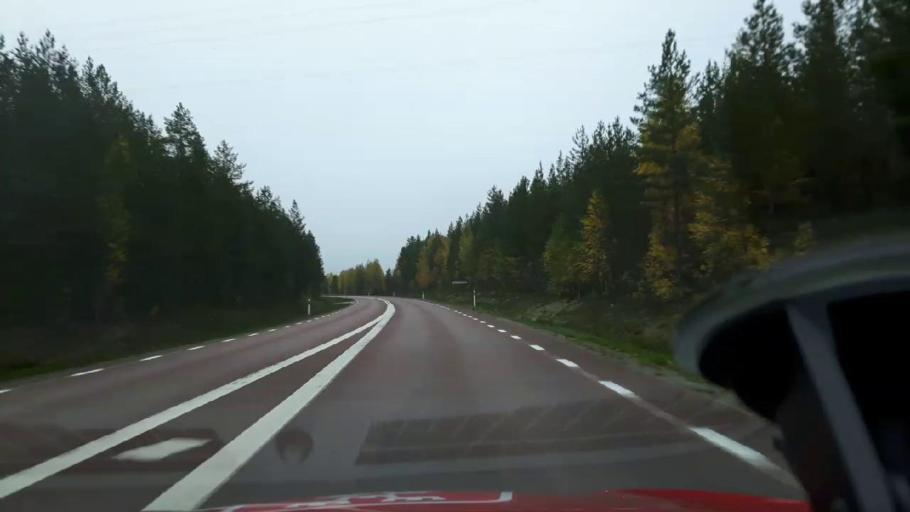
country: SE
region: Jaemtland
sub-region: Bergs Kommun
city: Hoverberg
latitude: 62.6193
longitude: 14.3761
